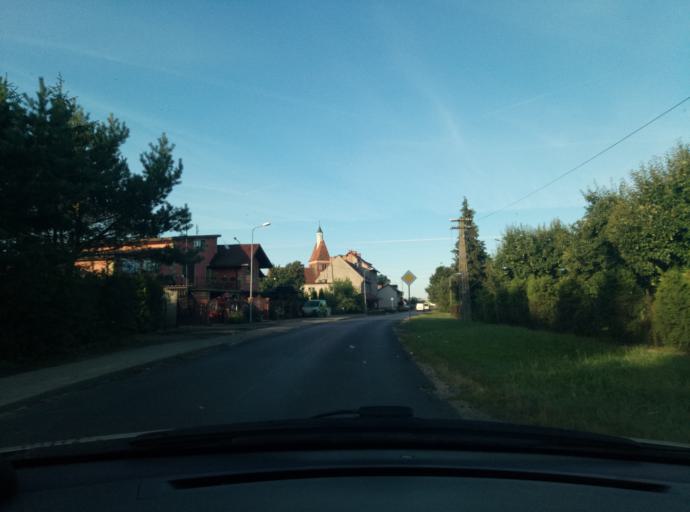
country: PL
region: Kujawsko-Pomorskie
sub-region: Powiat brodnicki
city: Jablonowo Pomorskie
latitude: 53.3964
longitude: 19.1587
